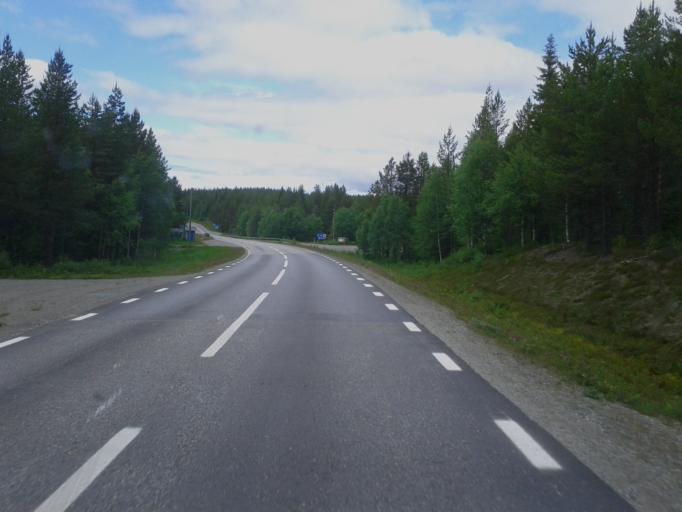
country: SE
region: Vaesterbotten
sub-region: Storumans Kommun
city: Fristad
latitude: 65.3820
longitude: 16.5100
